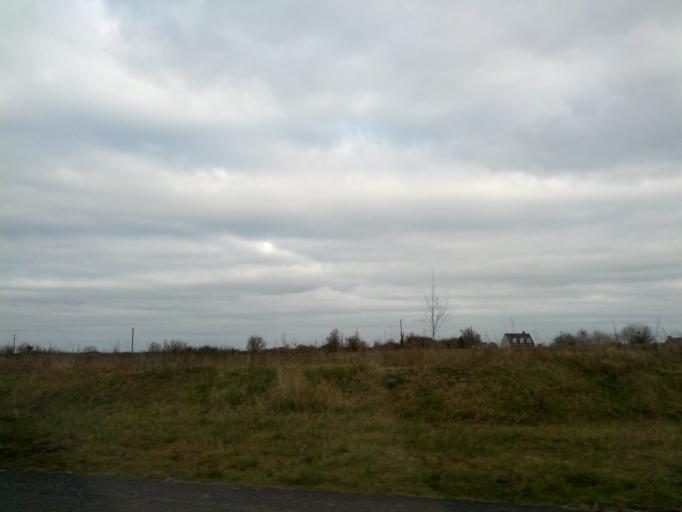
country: IE
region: Connaught
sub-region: County Galway
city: Gort
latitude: 53.1630
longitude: -8.8504
